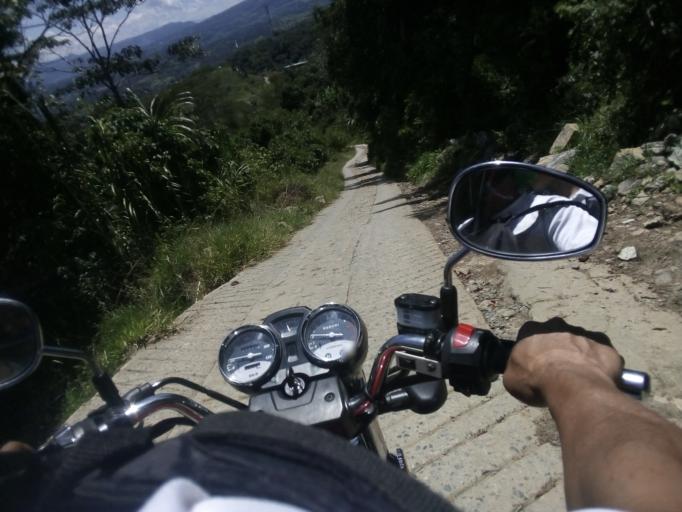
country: CO
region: Santander
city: Guepsa
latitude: 6.0116
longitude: -73.5553
